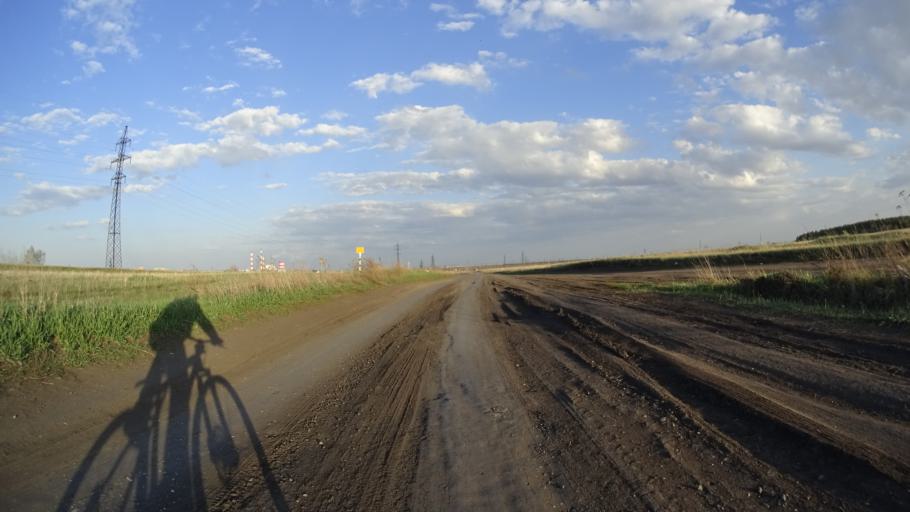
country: RU
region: Chelyabinsk
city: Troitsk
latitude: 54.0506
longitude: 61.5938
